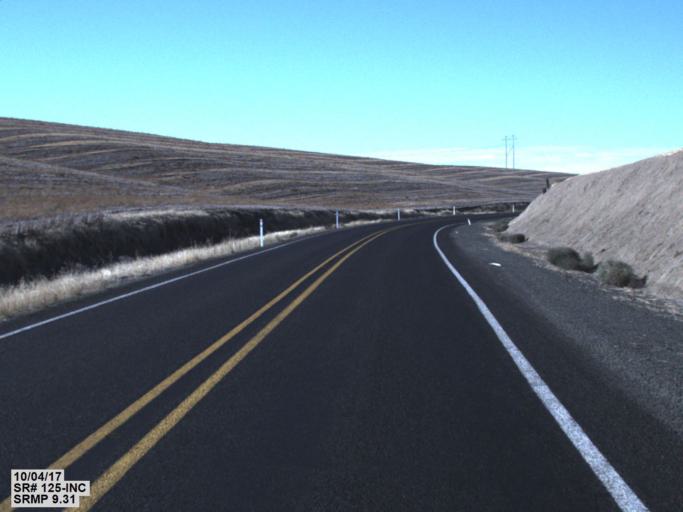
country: US
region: Washington
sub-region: Walla Walla County
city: Walla Walla
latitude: 46.1081
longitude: -118.3727
